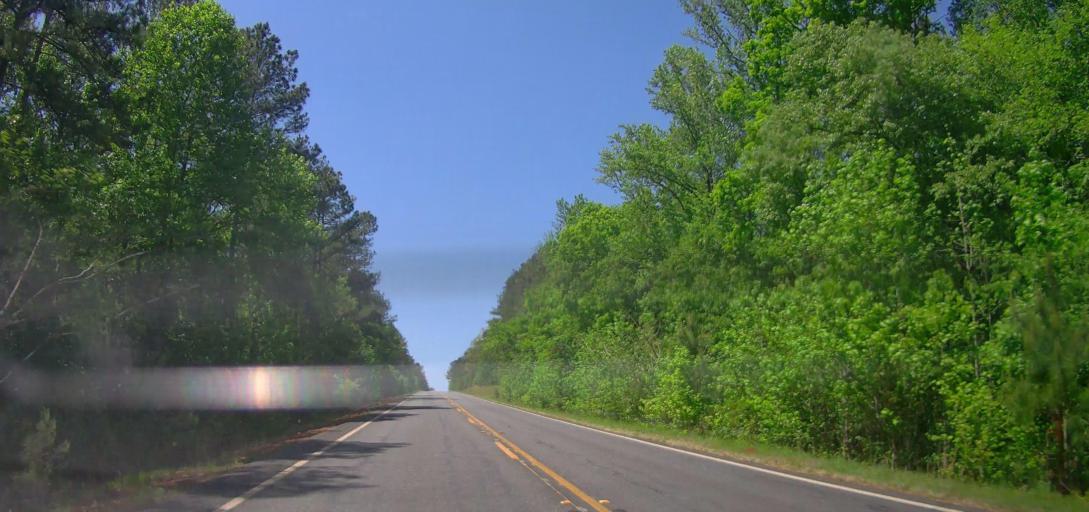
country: US
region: Georgia
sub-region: Putnam County
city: Eatonton
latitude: 33.2123
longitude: -83.4804
